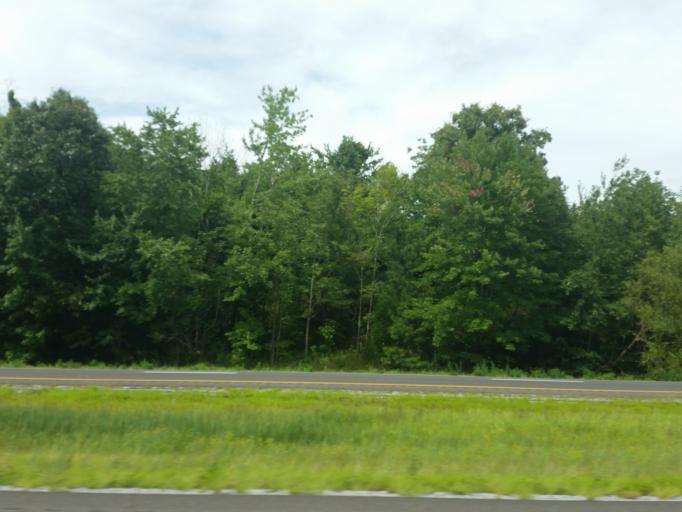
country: US
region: Kentucky
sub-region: Marshall County
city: Calvert City
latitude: 36.9908
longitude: -88.3877
